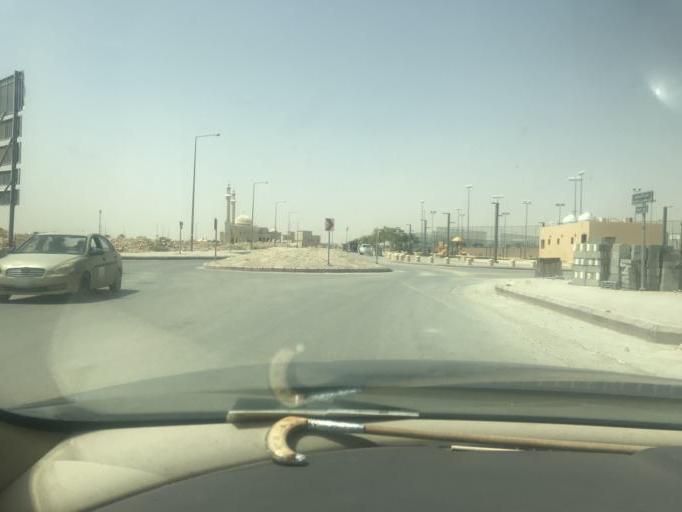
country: SA
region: Ar Riyad
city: Riyadh
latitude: 24.7876
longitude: 46.5807
